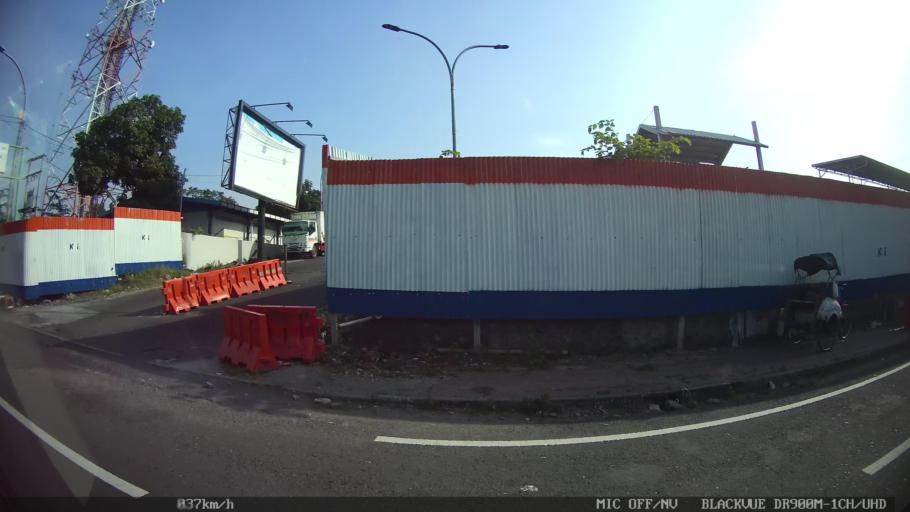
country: ID
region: Daerah Istimewa Yogyakarta
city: Yogyakarta
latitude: -7.7895
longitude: 110.3597
